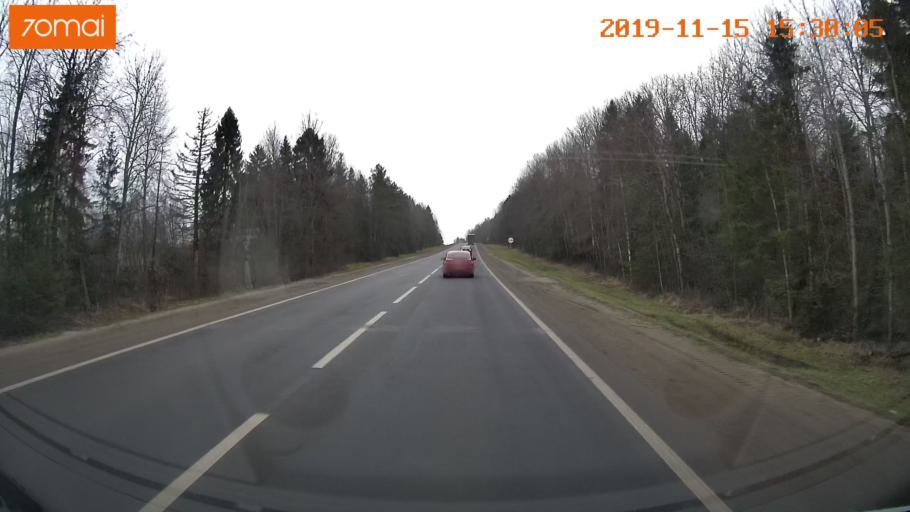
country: RU
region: Jaroslavl
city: Danilov
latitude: 58.1136
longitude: 40.1153
